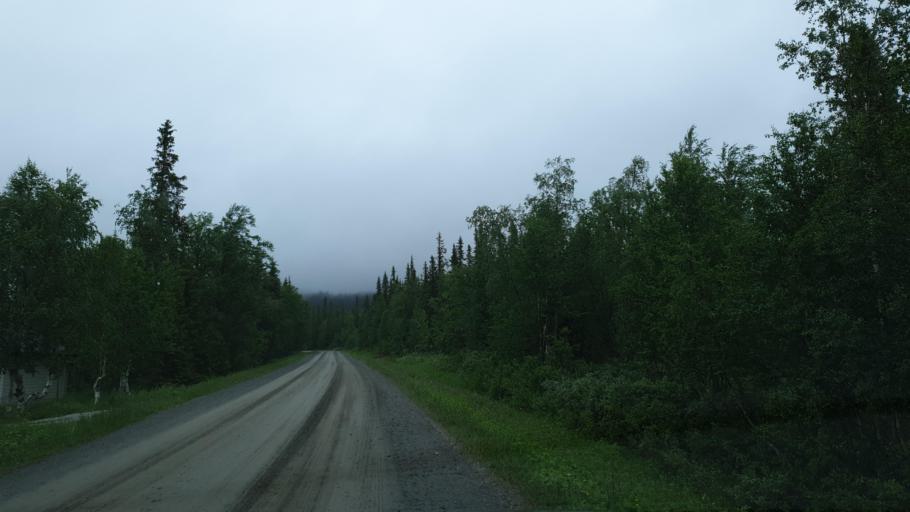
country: SE
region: Vaesterbotten
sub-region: Vilhelmina Kommun
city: Sjoberg
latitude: 65.3371
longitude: 15.8739
